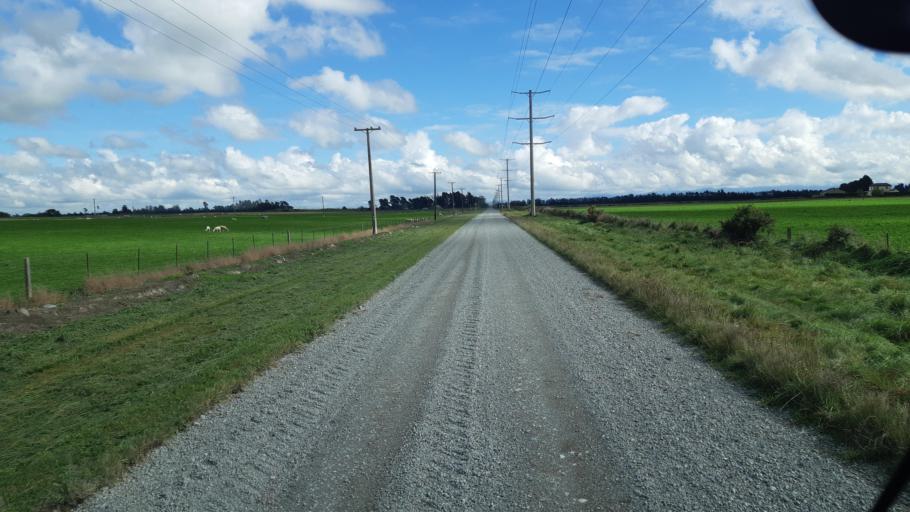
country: NZ
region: Canterbury
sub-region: Selwyn District
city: Darfield
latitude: -43.4728
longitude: 172.2485
